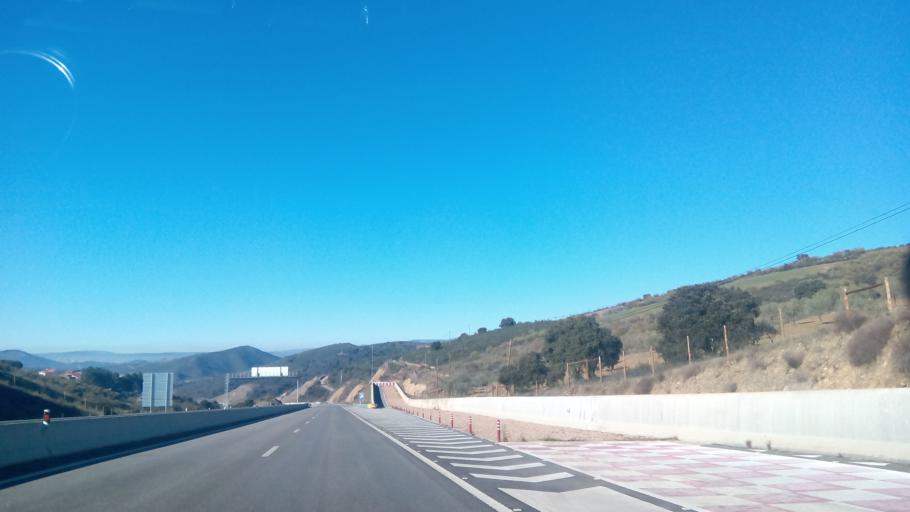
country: PT
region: Braganca
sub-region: Braganca Municipality
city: Braganca
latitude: 41.7599
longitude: -6.6468
